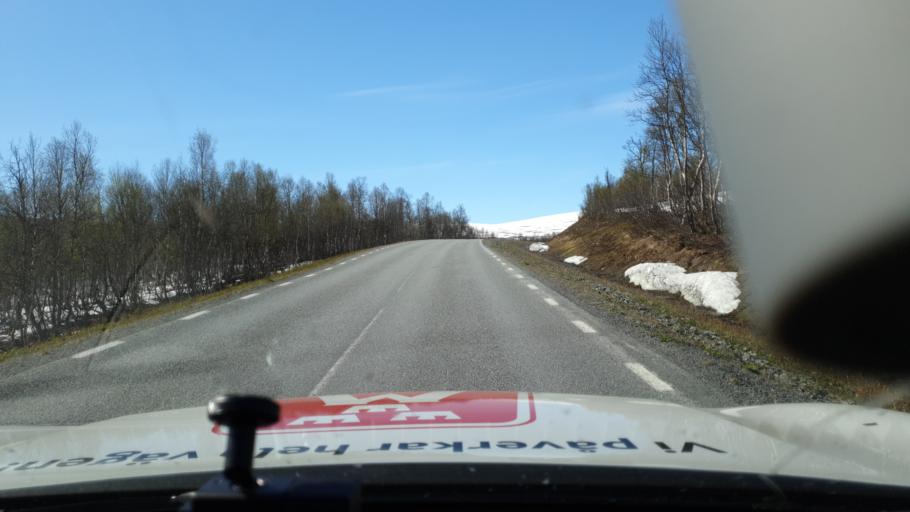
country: NO
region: Nordland
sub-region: Hattfjelldal
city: Hattfjelldal
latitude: 65.7020
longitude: 14.5991
